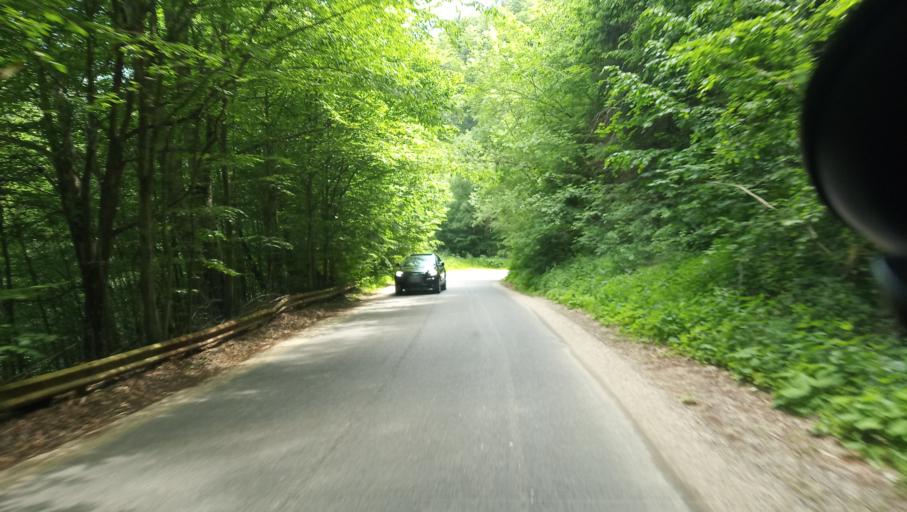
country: RO
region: Cluj
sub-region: Comuna Maguri-Racatau
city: Maguri-Racatau
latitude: 46.7061
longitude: 23.2257
